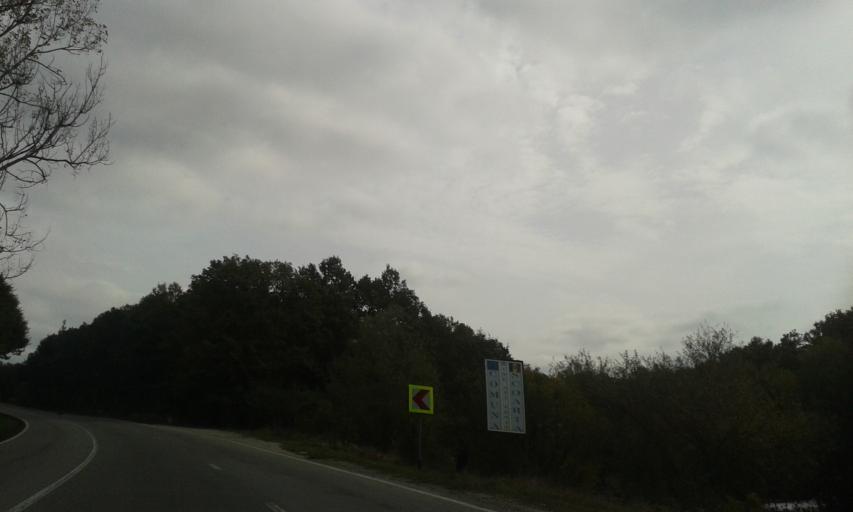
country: RO
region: Gorj
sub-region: Comuna Balanesti
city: Balanesti
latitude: 45.0327
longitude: 23.3783
